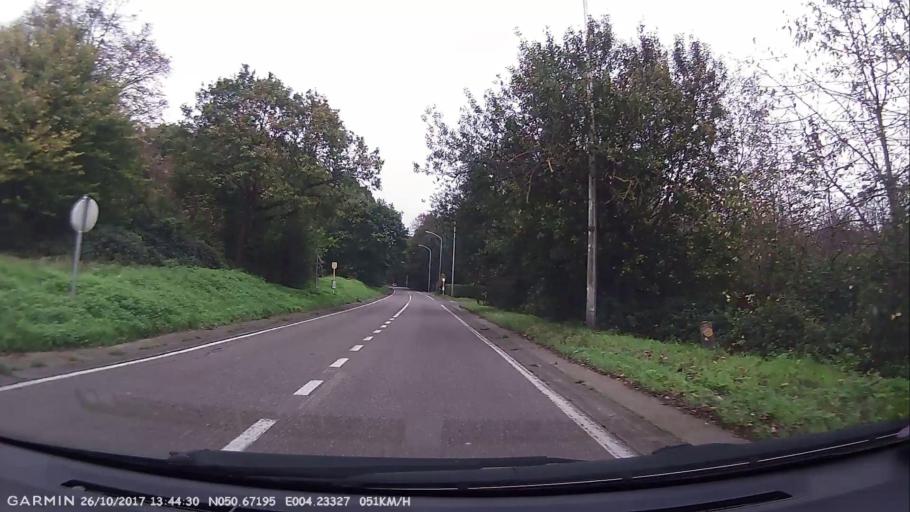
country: BE
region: Wallonia
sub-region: Province du Brabant Wallon
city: Tubize
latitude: 50.6718
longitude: 4.2333
